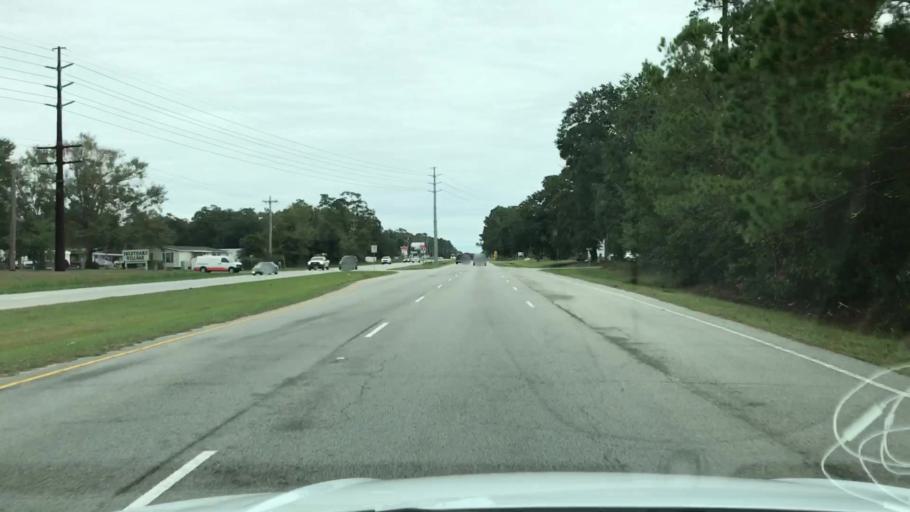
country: US
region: South Carolina
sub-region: Georgetown County
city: Murrells Inlet
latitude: 33.5313
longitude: -79.0607
